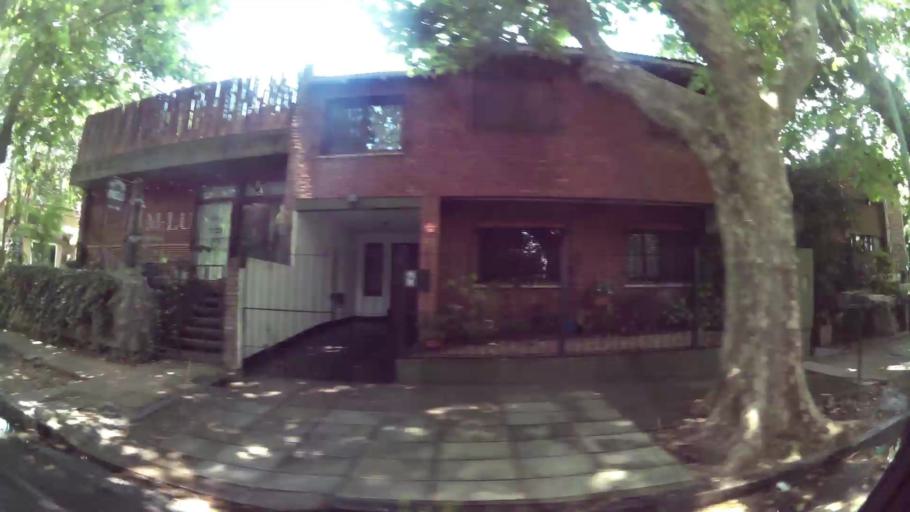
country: AR
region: Buenos Aires
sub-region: Partido de Tigre
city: Tigre
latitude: -34.4173
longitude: -58.5844
